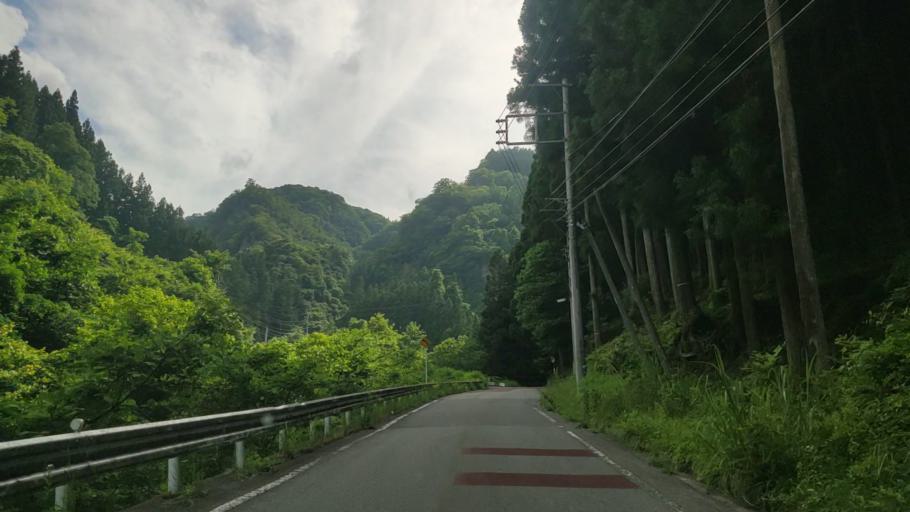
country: JP
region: Gunma
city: Tomioka
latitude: 36.1420
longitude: 138.7266
